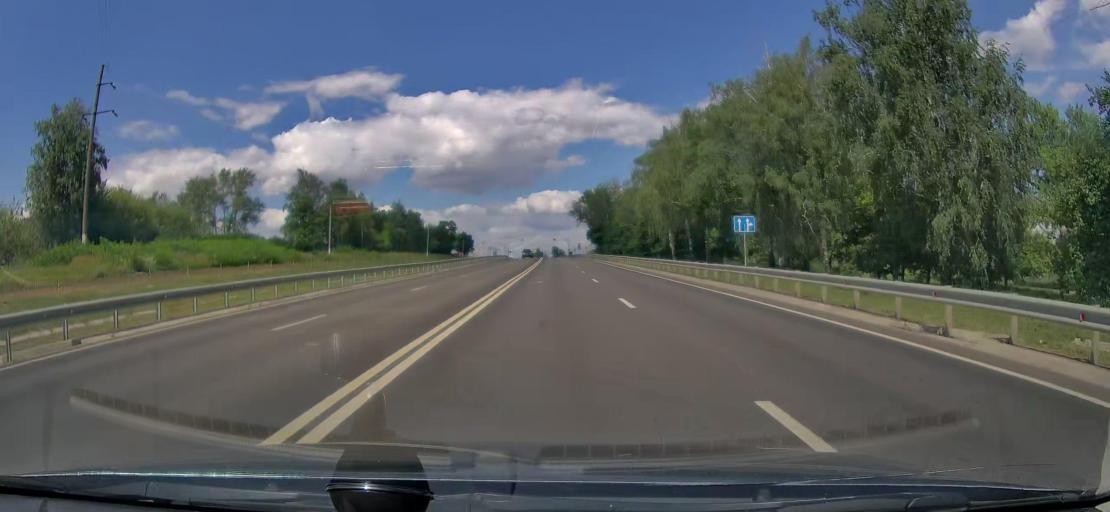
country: RU
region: Kursk
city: Zolotukhino
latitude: 51.9582
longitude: 36.3054
